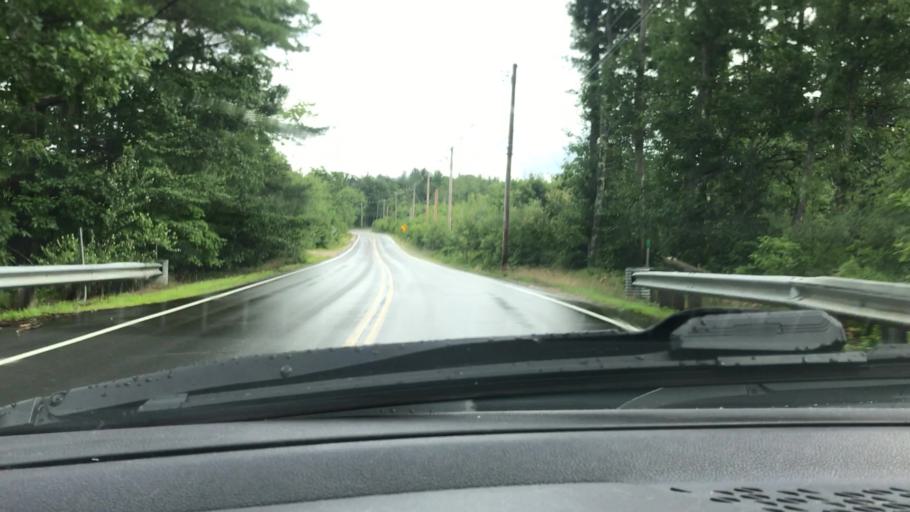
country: US
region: New Hampshire
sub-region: Merrimack County
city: Epsom
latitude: 43.2112
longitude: -71.2840
